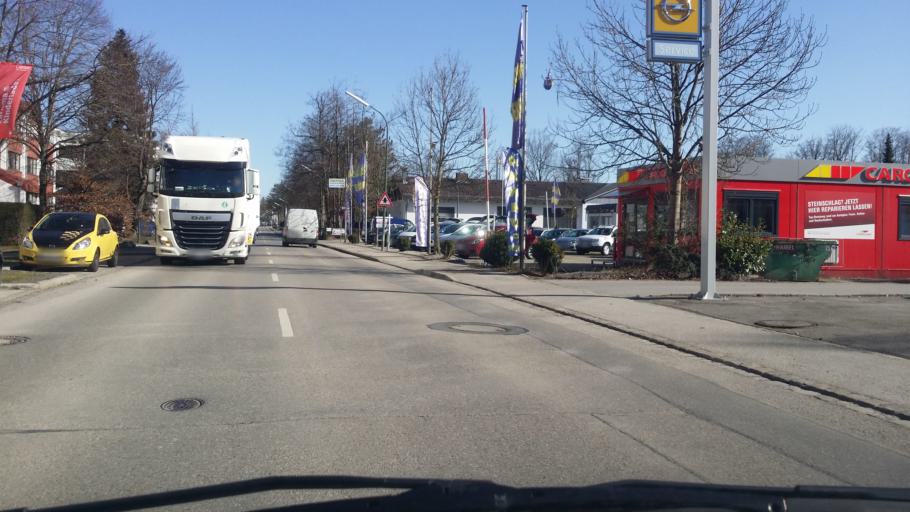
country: DE
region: Bavaria
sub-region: Upper Bavaria
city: Geretsried
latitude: 47.8553
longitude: 11.4891
